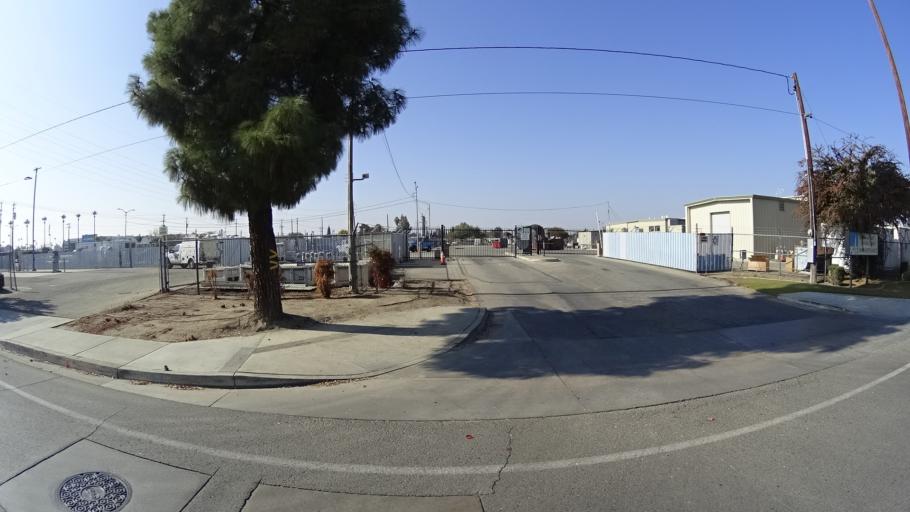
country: US
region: California
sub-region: Kern County
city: Greenfield
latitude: 35.3151
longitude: -119.0391
